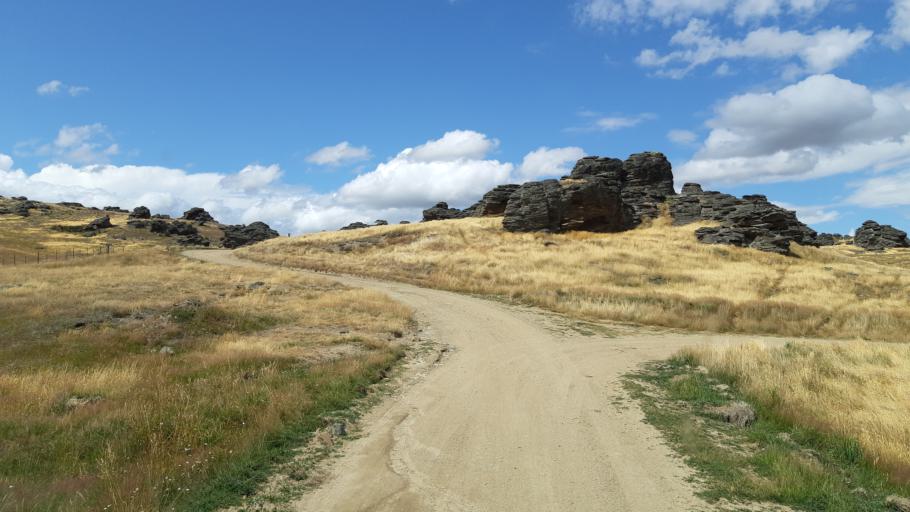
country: NZ
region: Otago
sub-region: Queenstown-Lakes District
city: Wanaka
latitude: -45.2973
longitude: 169.7466
